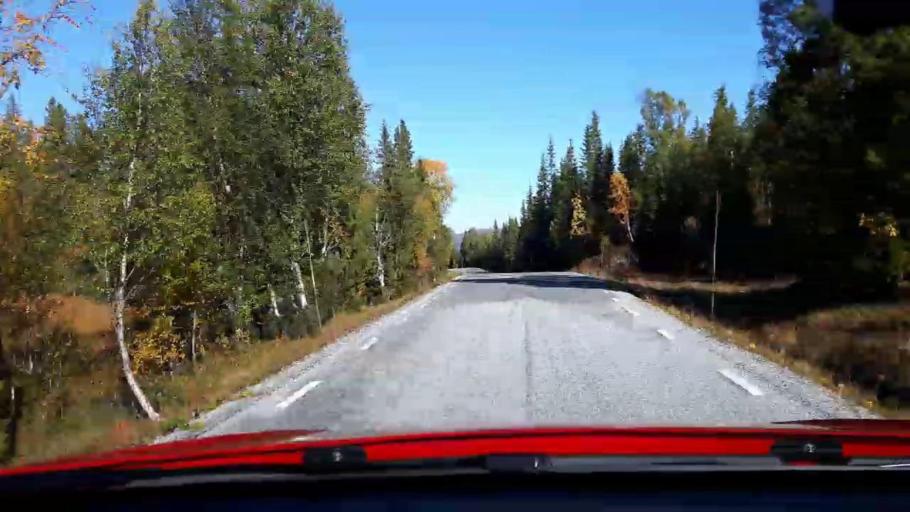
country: NO
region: Nord-Trondelag
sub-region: Lierne
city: Sandvika
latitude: 64.6206
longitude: 13.6972
